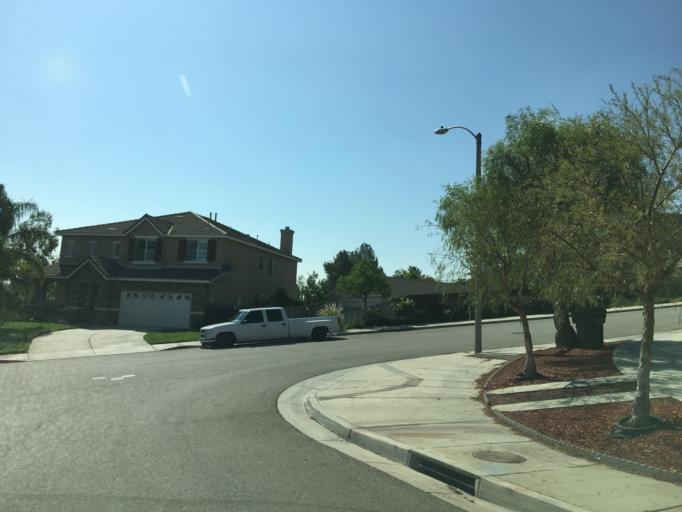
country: US
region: California
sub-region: Los Angeles County
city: Castaic
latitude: 34.4884
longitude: -118.6269
